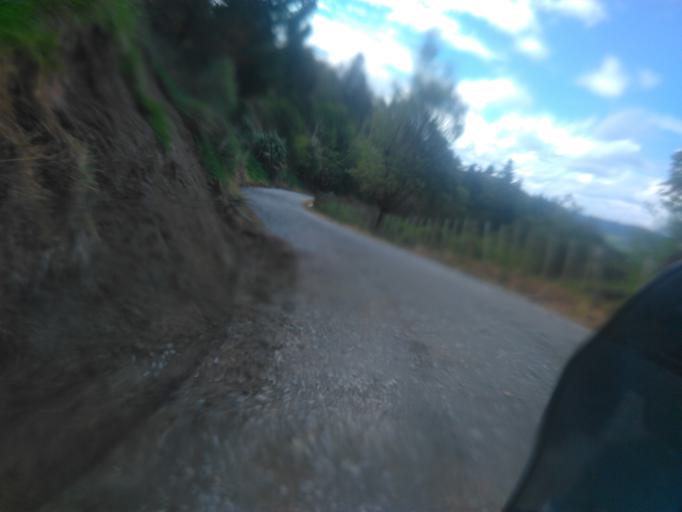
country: NZ
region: Hawke's Bay
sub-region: Wairoa District
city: Wairoa
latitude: -38.7775
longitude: 177.6299
